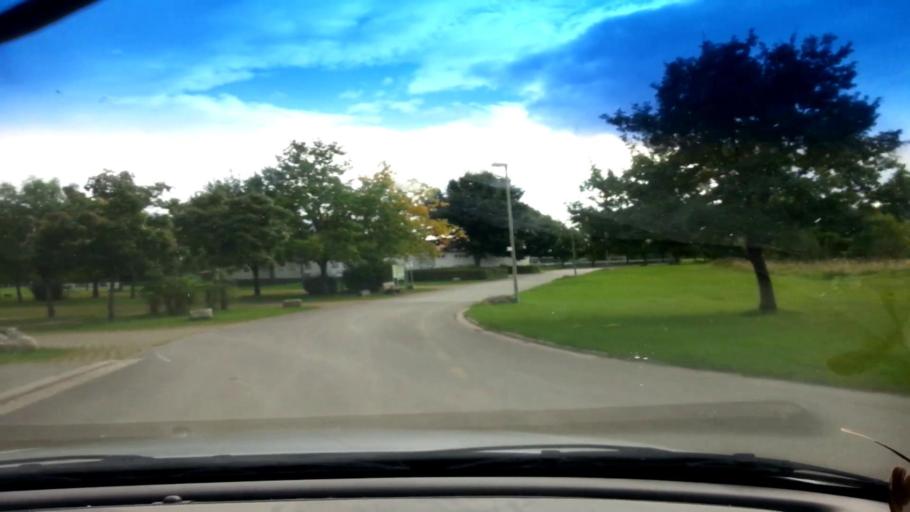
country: DE
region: Bavaria
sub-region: Upper Franconia
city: Kemmern
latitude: 49.9506
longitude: 10.8726
